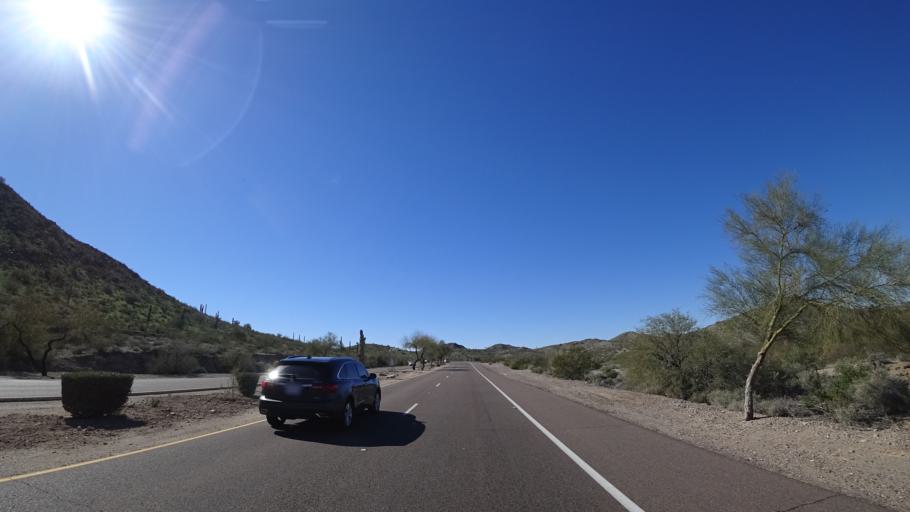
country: US
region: Arizona
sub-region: Maricopa County
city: Goodyear
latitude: 33.3819
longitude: -112.3943
